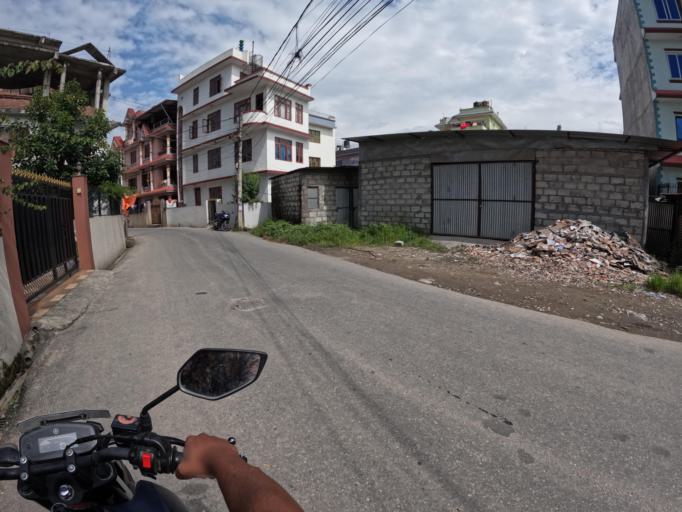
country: NP
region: Central Region
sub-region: Bagmati Zone
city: Kathmandu
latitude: 27.6882
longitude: 85.3745
